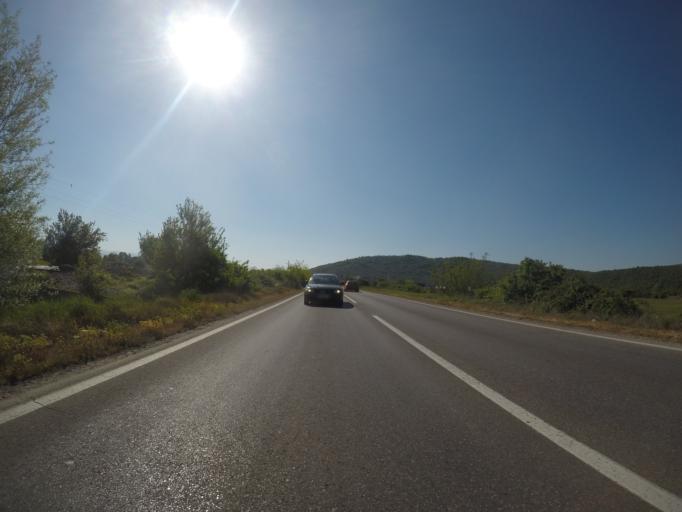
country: ME
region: Danilovgrad
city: Danilovgrad
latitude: 42.5145
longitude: 19.1255
